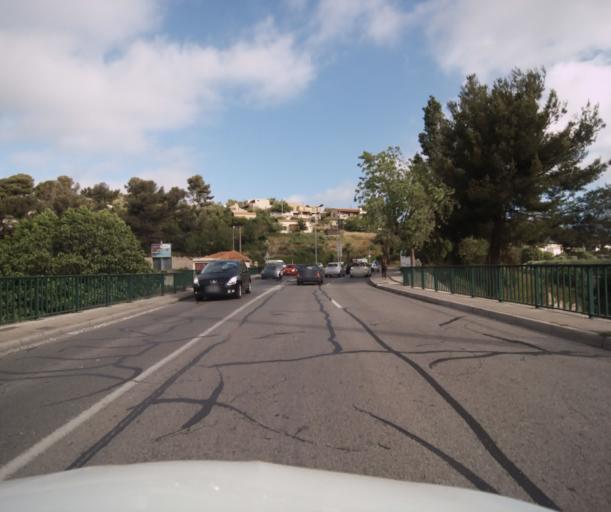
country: FR
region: Provence-Alpes-Cote d'Azur
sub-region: Departement du Var
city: Ollioules
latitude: 43.1281
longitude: 5.8448
